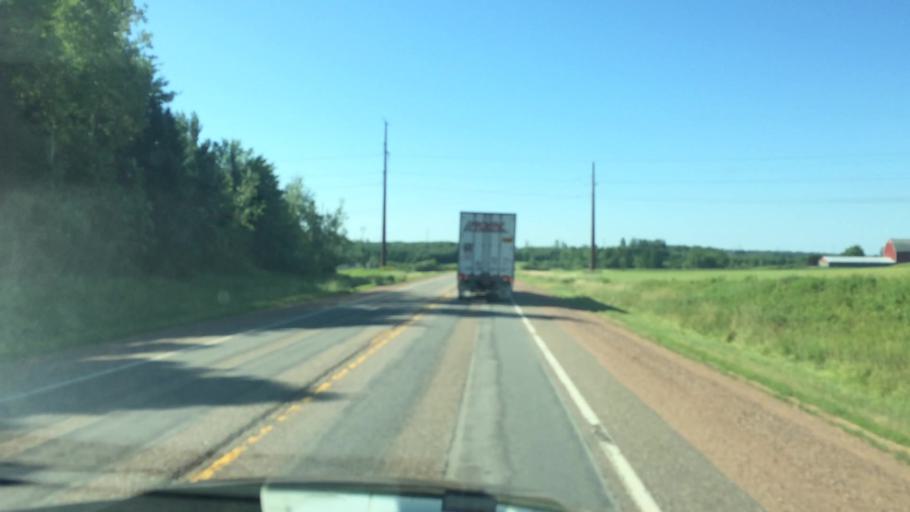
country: US
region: Wisconsin
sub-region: Marathon County
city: Athens
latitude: 44.9362
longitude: -90.0791
